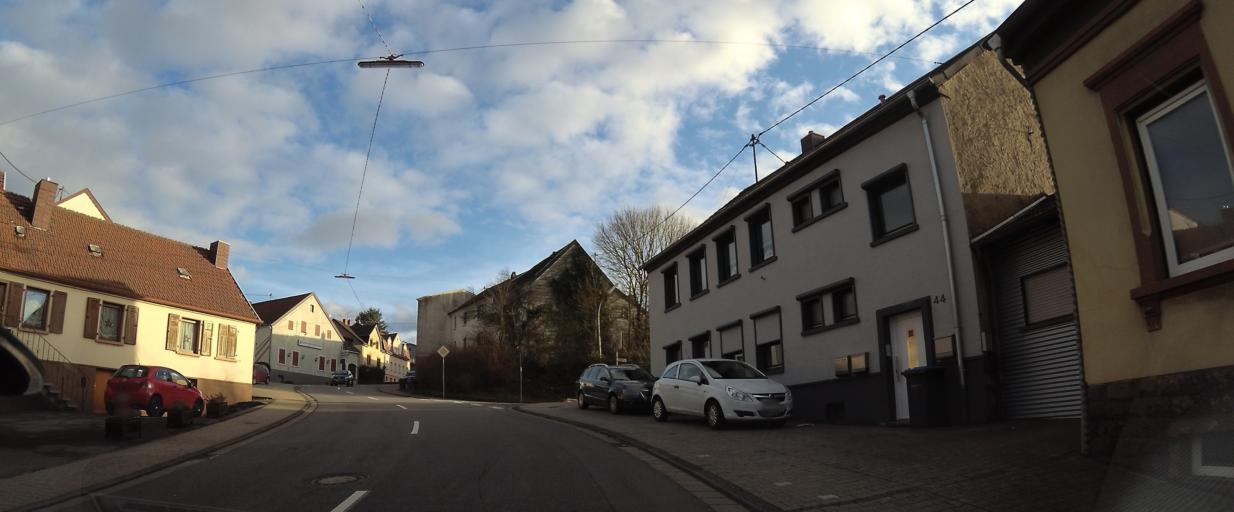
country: DE
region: Saarland
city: Illingen
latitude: 49.3735
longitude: 7.0843
